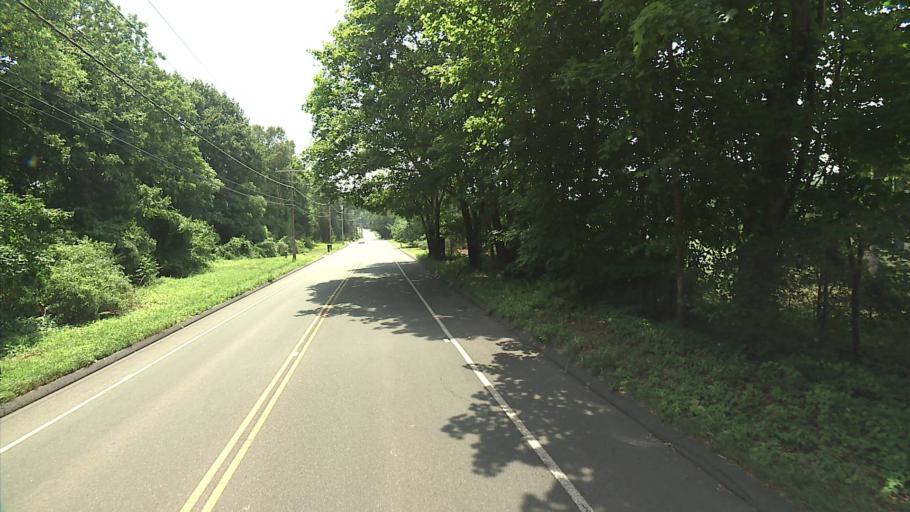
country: US
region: Connecticut
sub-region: New Haven County
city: Madison
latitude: 41.3085
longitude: -72.5927
